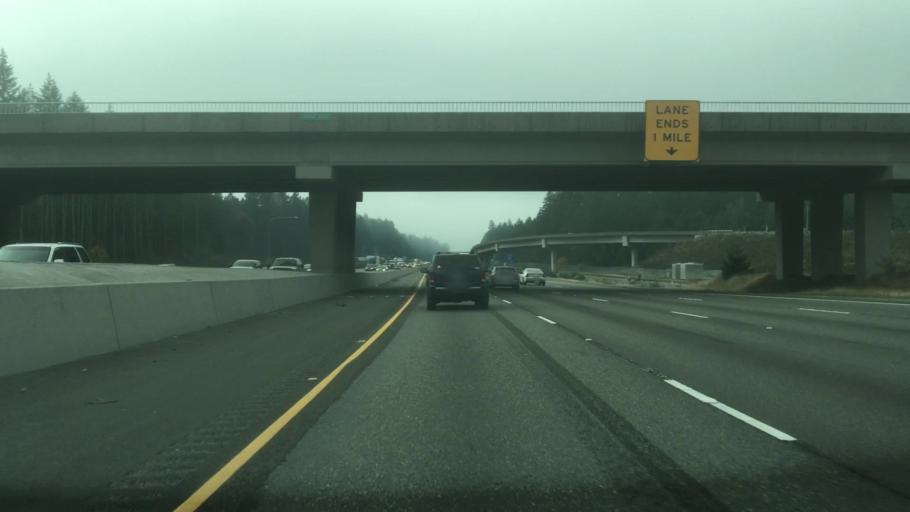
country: US
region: Washington
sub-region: Pierce County
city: DuPont
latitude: 47.0882
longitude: -122.6444
